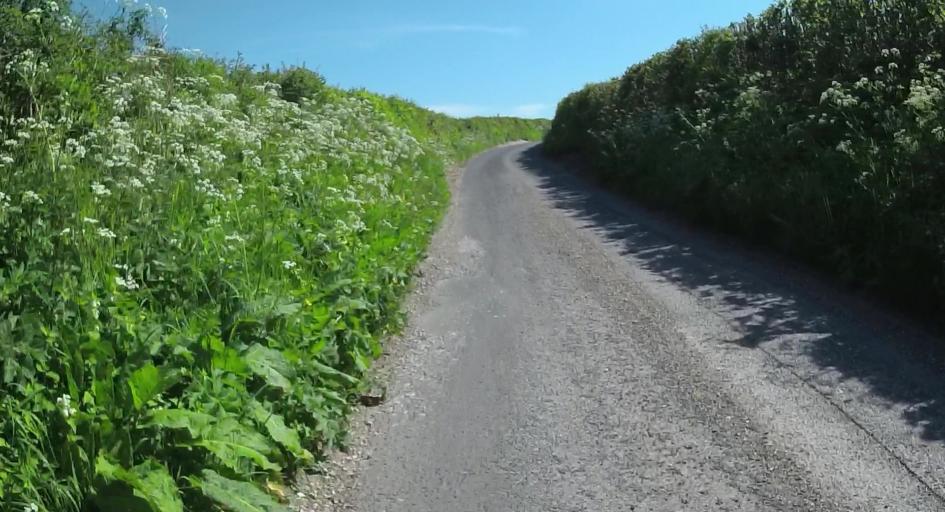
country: GB
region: England
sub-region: Hampshire
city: Kings Worthy
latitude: 51.0782
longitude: -1.2703
